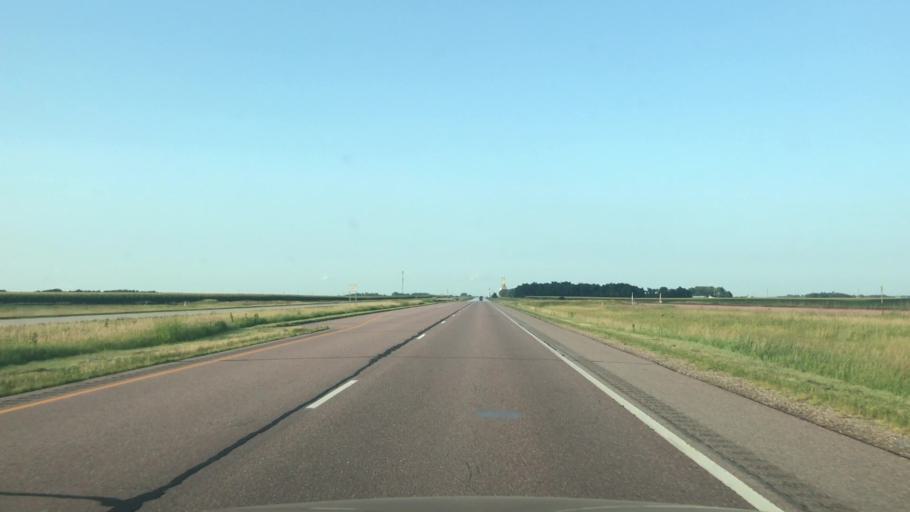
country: US
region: Minnesota
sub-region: Jackson County
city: Lakefield
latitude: 43.7523
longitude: -95.3887
